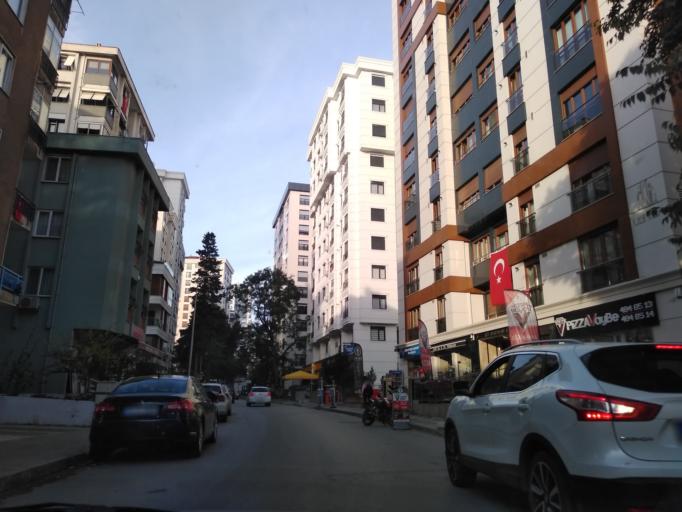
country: TR
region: Istanbul
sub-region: Atasehir
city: Atasehir
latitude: 40.9670
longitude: 29.0877
